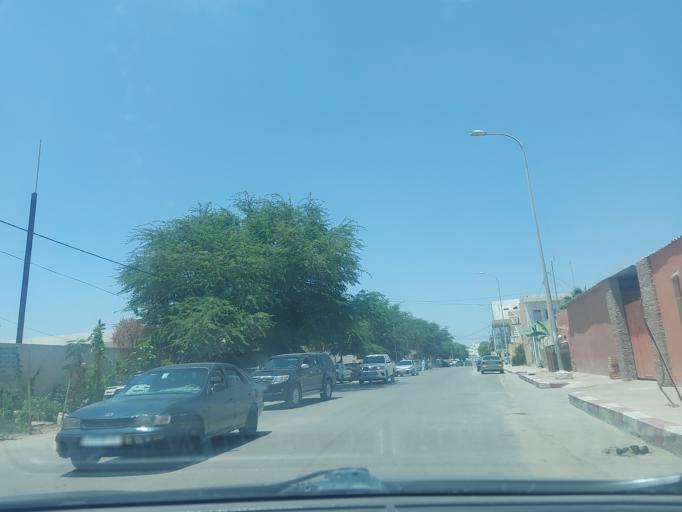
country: MR
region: Nouakchott
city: Nouakchott
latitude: 18.0887
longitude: -15.9828
